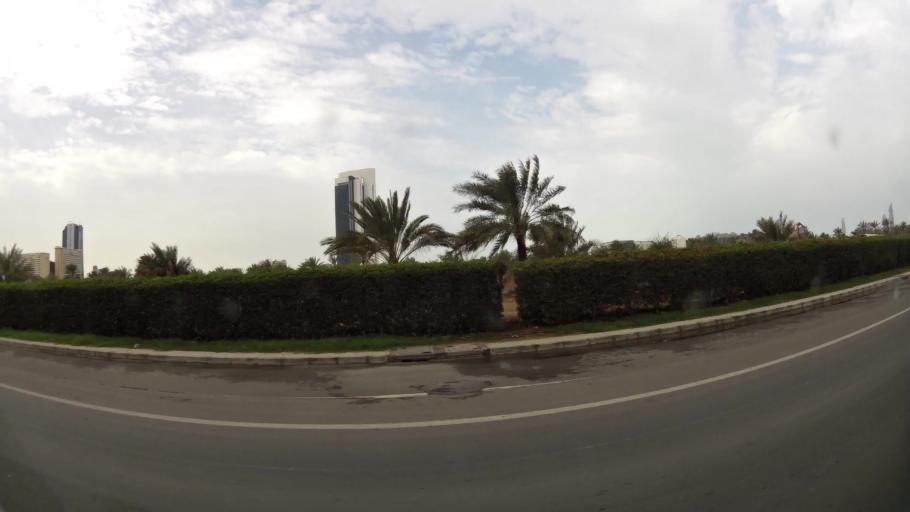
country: AE
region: Abu Dhabi
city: Abu Dhabi
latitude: 24.4642
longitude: 54.3973
